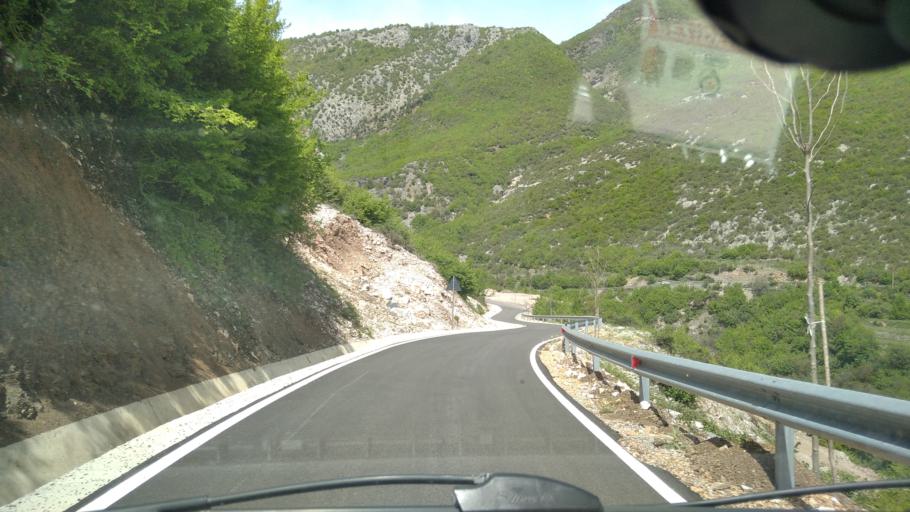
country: AL
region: Shkoder
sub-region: Rrethi i Shkodres
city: Guri i Zi
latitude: 42.1279
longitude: 19.6148
